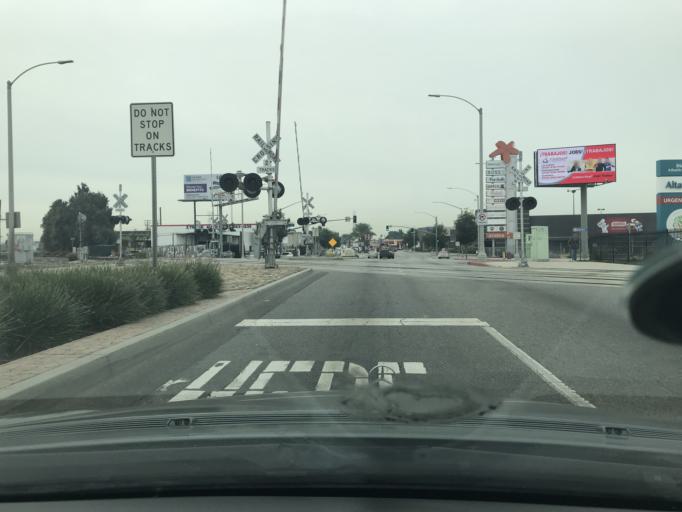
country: US
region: California
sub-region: Los Angeles County
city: Cudahy
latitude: 33.9548
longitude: -118.1838
